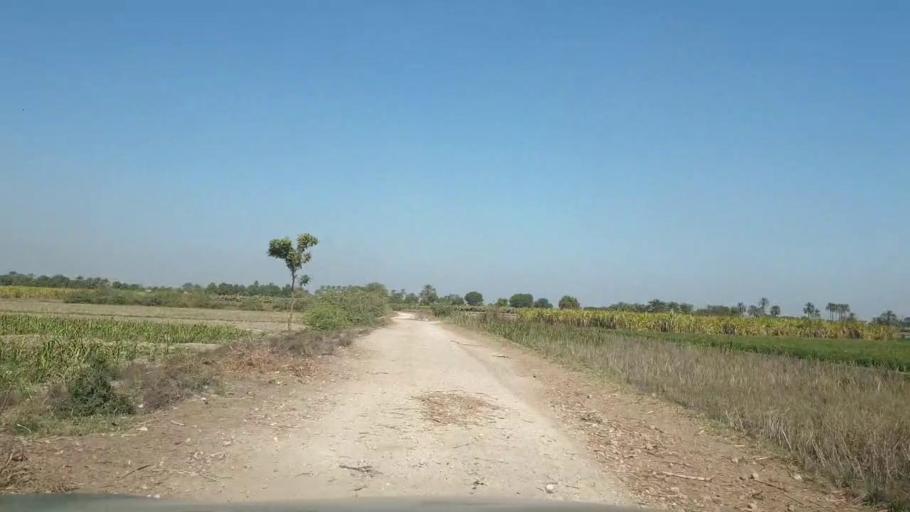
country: PK
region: Sindh
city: Tando Adam
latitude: 25.6311
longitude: 68.6751
